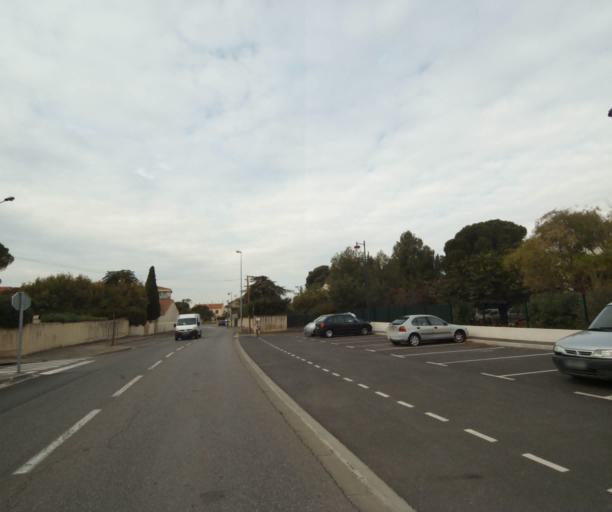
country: FR
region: Provence-Alpes-Cote d'Azur
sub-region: Departement des Bouches-du-Rhone
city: Saint-Victoret
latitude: 43.4189
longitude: 5.2467
